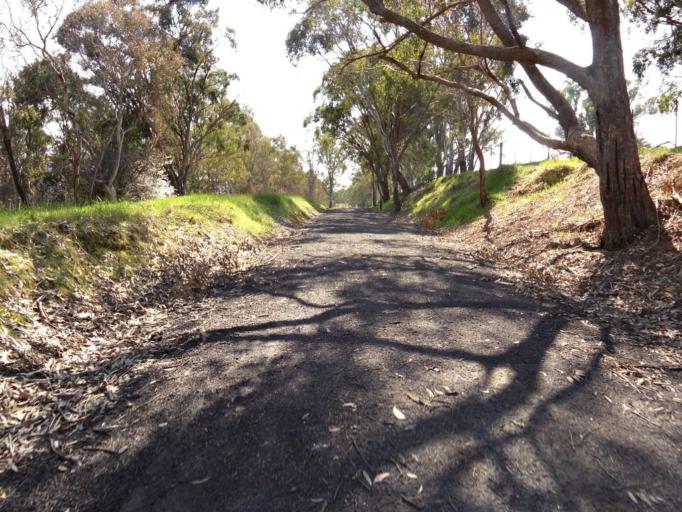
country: AU
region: Victoria
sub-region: Murrindindi
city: Alexandra
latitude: -37.1360
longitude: 145.5918
